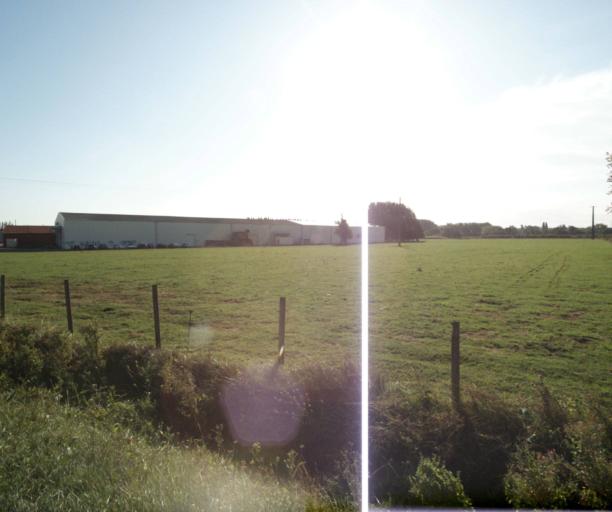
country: FR
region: Nord-Pas-de-Calais
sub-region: Departement du Nord
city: Sainghin-en-Melantois
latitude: 50.5754
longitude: 3.1732
